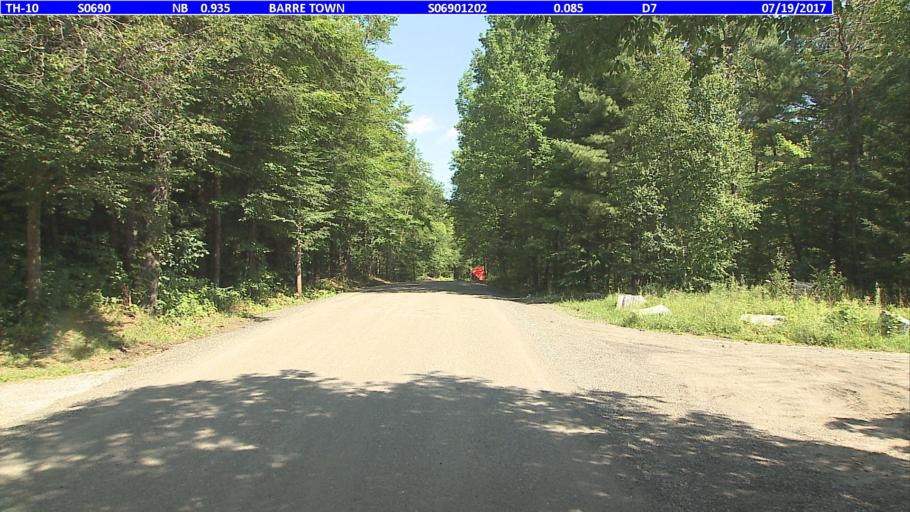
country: US
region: Vermont
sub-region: Washington County
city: South Barre
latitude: 44.1449
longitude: -72.4929
